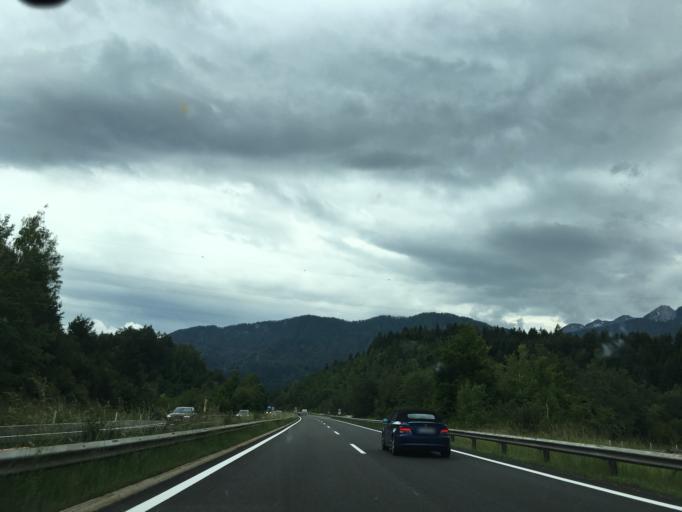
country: AT
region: Carinthia
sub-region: Politischer Bezirk Villach Land
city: Rosegg
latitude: 46.5602
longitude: 14.0061
